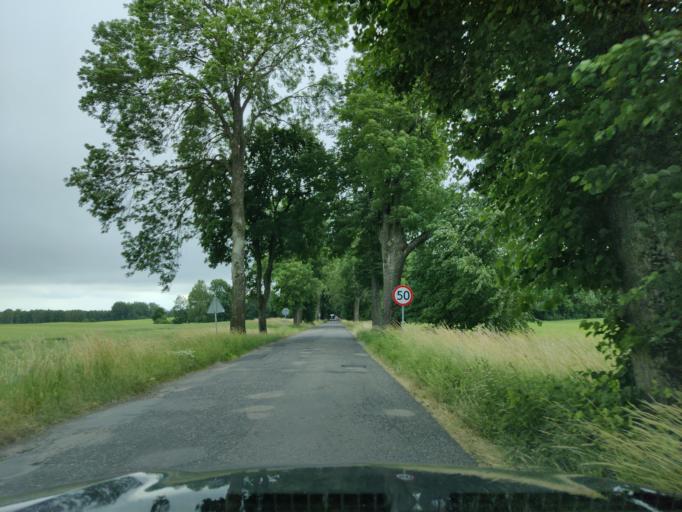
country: PL
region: Warmian-Masurian Voivodeship
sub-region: Powiat gizycki
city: Ryn
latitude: 53.9192
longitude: 21.5546
